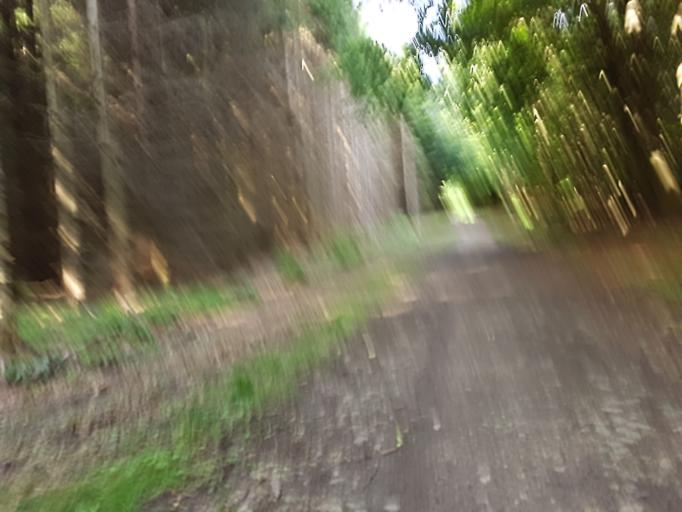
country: DK
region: Capital Region
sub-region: Egedal Kommune
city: Ganlose
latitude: 55.7980
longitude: 12.2971
